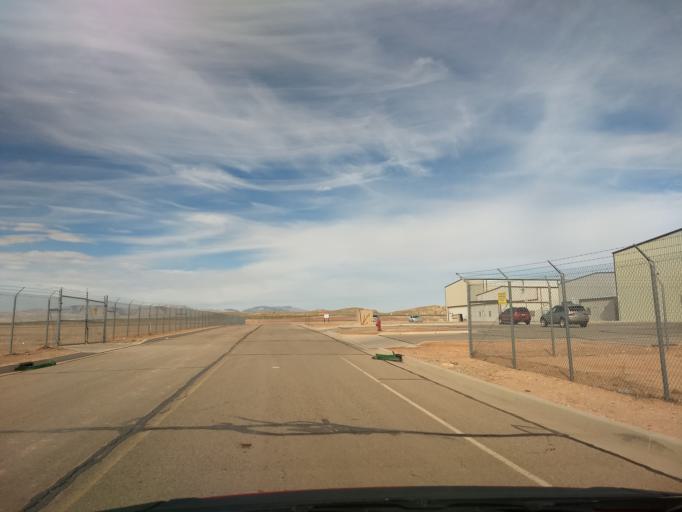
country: US
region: Utah
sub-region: Washington County
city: Washington
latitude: 37.0342
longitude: -113.5042
